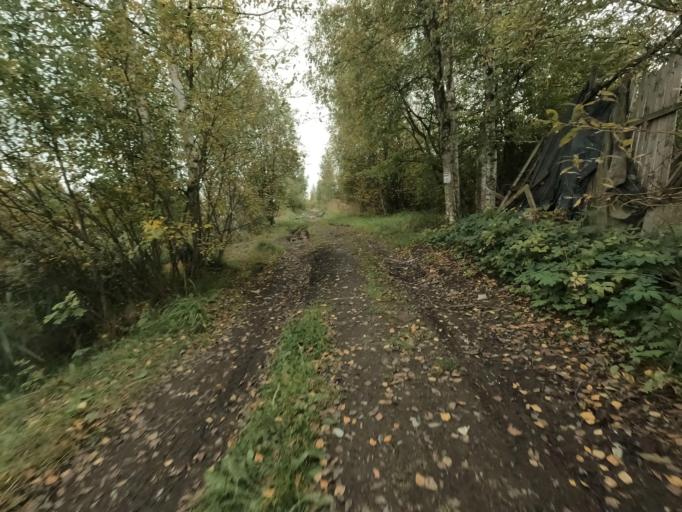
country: RU
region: St.-Petersburg
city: Sapernyy
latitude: 59.7775
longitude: 30.6418
